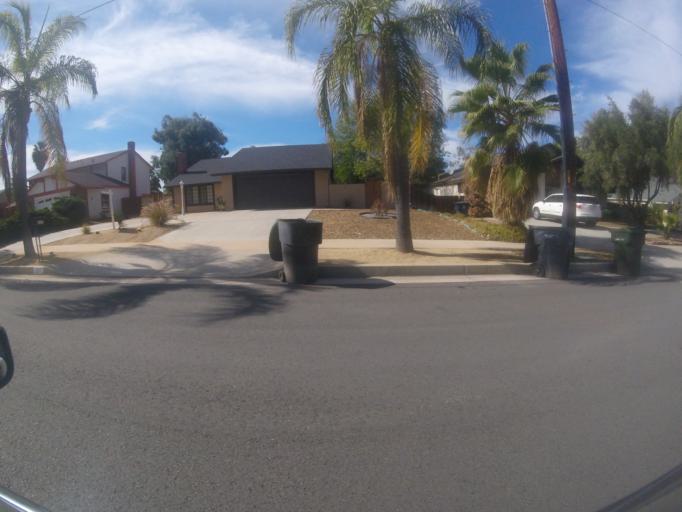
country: US
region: California
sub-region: San Bernardino County
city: Mentone
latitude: 34.0581
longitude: -117.1477
